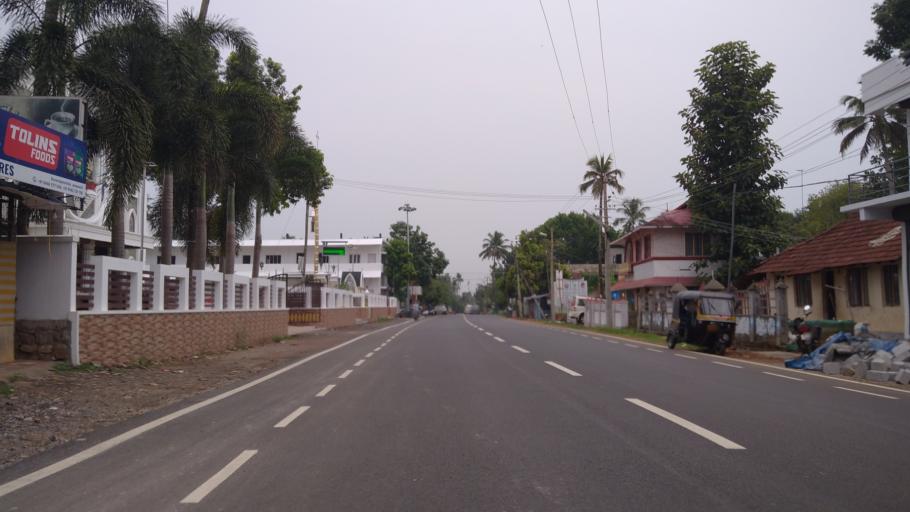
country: IN
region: Kerala
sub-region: Ernakulam
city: Angamali
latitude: 10.1791
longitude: 76.3980
